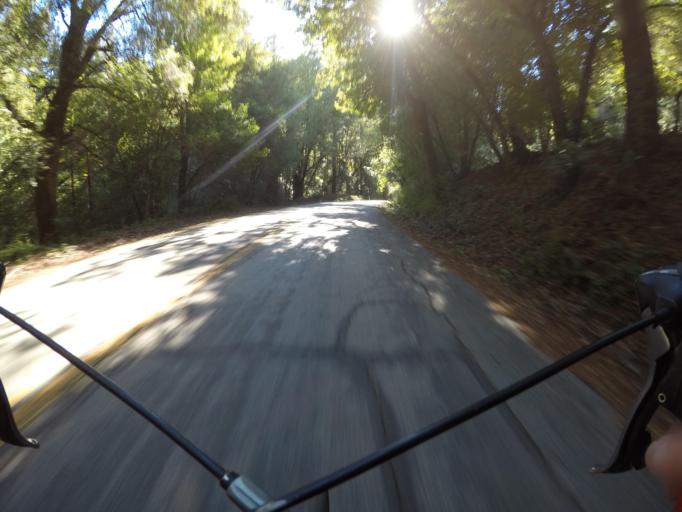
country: US
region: California
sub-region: Santa Cruz County
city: Scotts Valley
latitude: 37.1042
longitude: -121.9875
